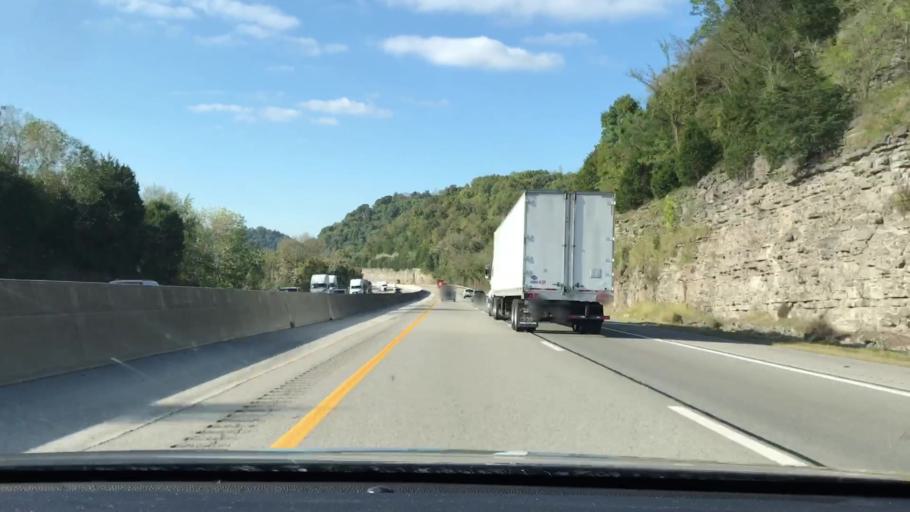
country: US
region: Tennessee
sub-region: Putnam County
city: Lafayette
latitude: 36.1098
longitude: -85.7699
